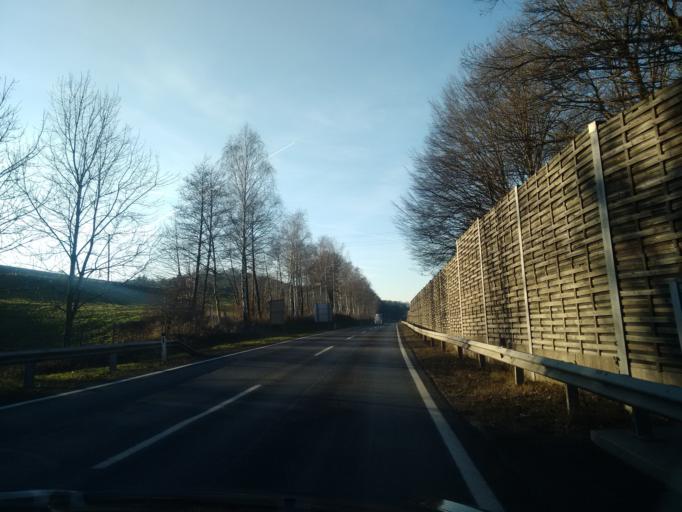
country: AT
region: Lower Austria
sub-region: Politischer Bezirk Sankt Polten
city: Neulengbach
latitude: 48.1820
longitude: 15.8845
